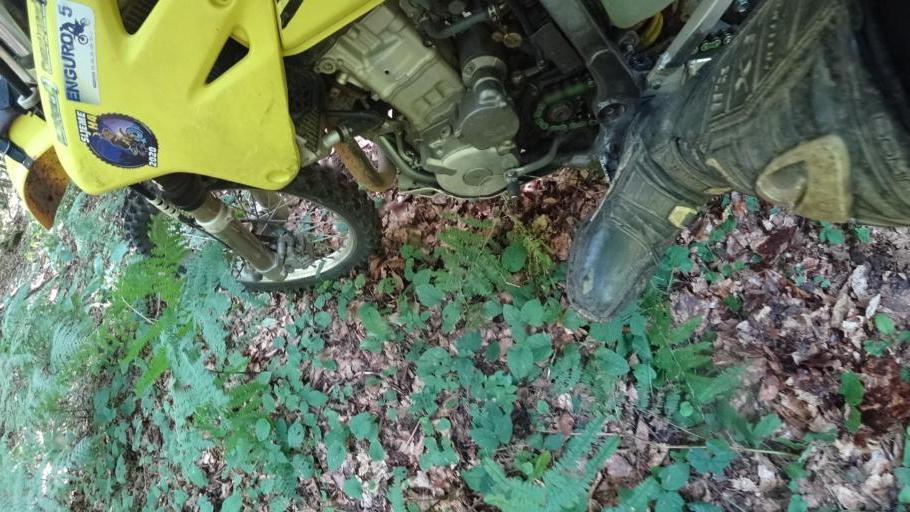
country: HR
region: Karlovacka
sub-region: Grad Ogulin
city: Ogulin
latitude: 45.2317
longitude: 15.1851
